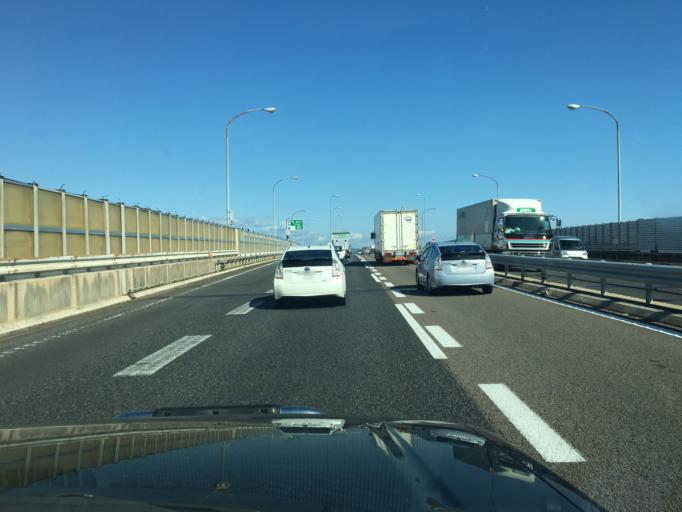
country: JP
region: Aichi
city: Kasugai
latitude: 35.2291
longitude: 136.9369
